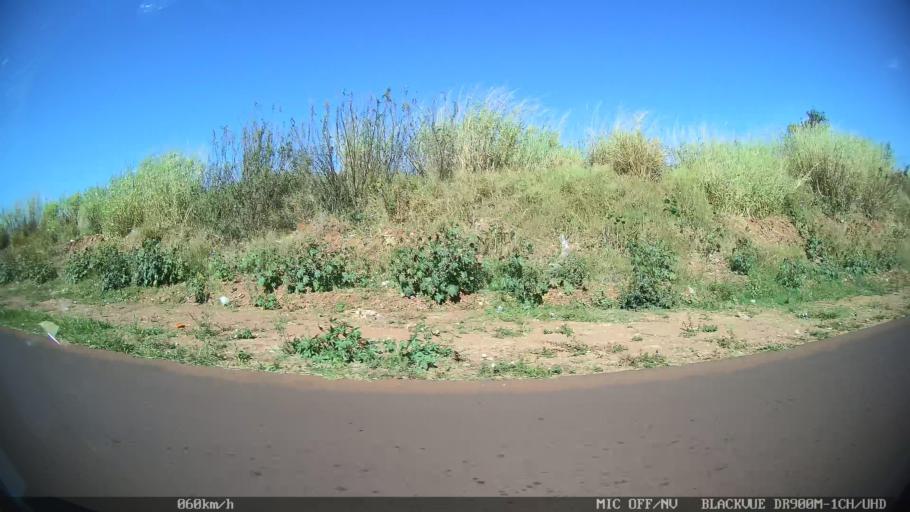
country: BR
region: Sao Paulo
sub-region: Batatais
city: Batatais
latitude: -20.8755
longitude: -47.5839
